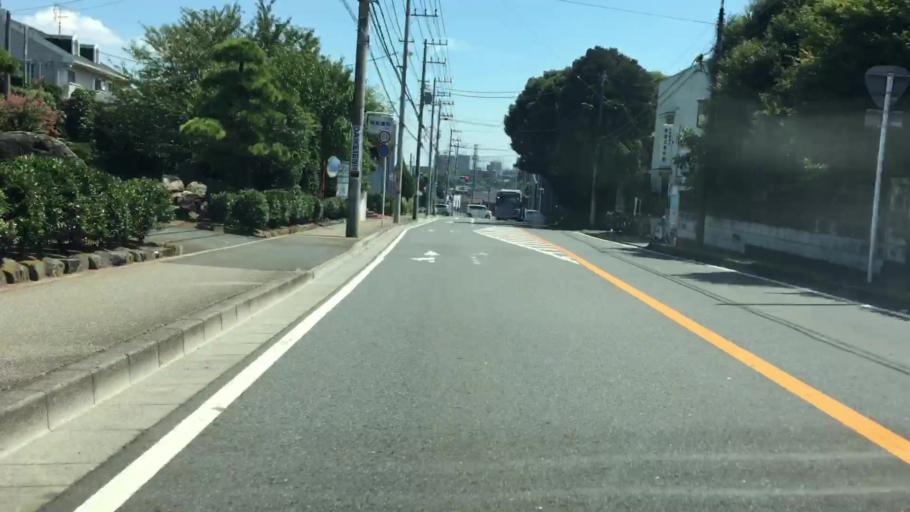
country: JP
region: Chiba
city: Matsudo
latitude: 35.7732
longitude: 139.9159
